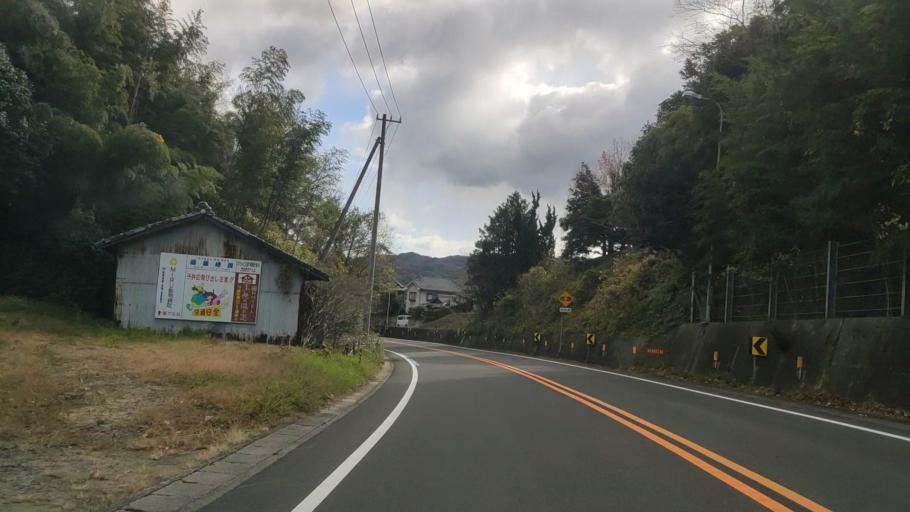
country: JP
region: Ehime
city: Hojo
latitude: 34.0605
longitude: 132.9160
